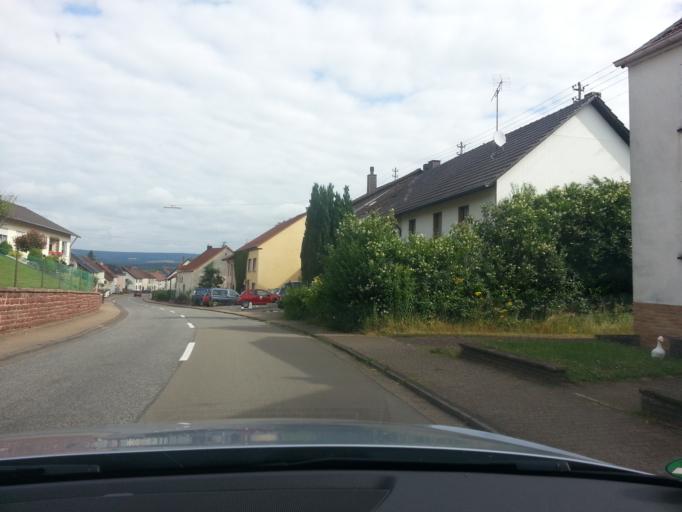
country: DE
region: Saarland
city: Losheim
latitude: 49.4841
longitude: 6.7828
